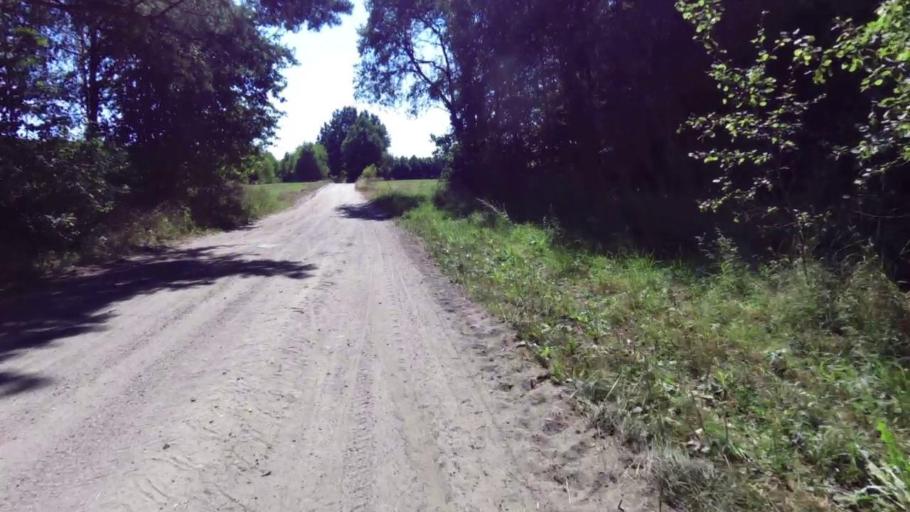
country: PL
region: West Pomeranian Voivodeship
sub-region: Powiat drawski
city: Zlocieniec
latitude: 53.5225
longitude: 16.0455
